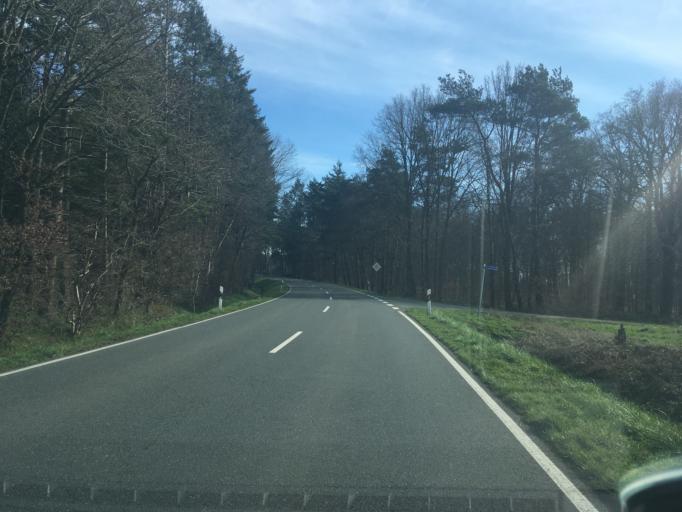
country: DE
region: North Rhine-Westphalia
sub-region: Regierungsbezirk Munster
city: Isselburg
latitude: 51.8454
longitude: 6.4793
